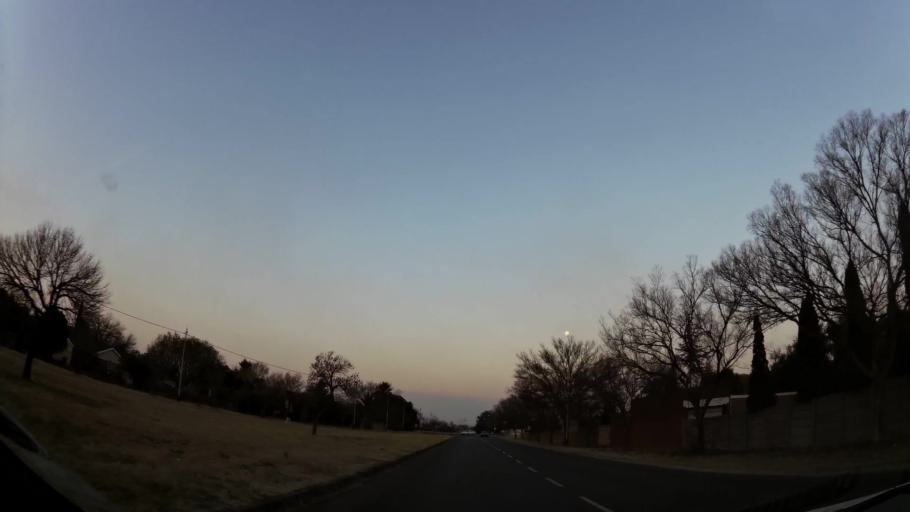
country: ZA
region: Gauteng
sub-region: Ekurhuleni Metropolitan Municipality
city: Nigel
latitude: -26.3534
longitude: 28.4375
